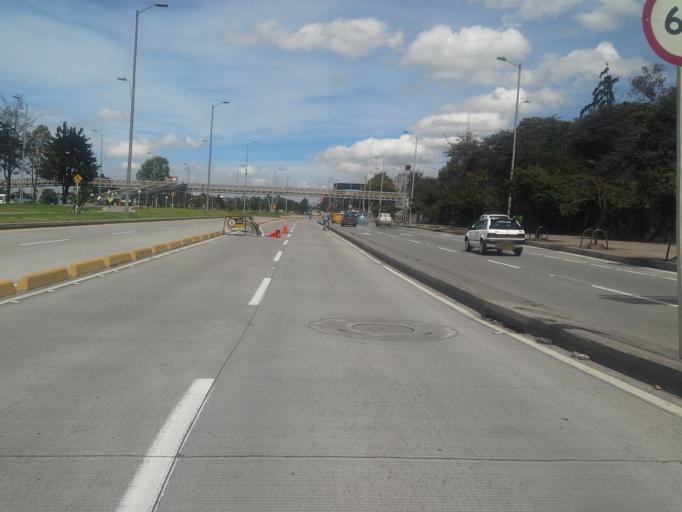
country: CO
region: Bogota D.C.
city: Bogota
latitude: 4.6837
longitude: -74.1228
